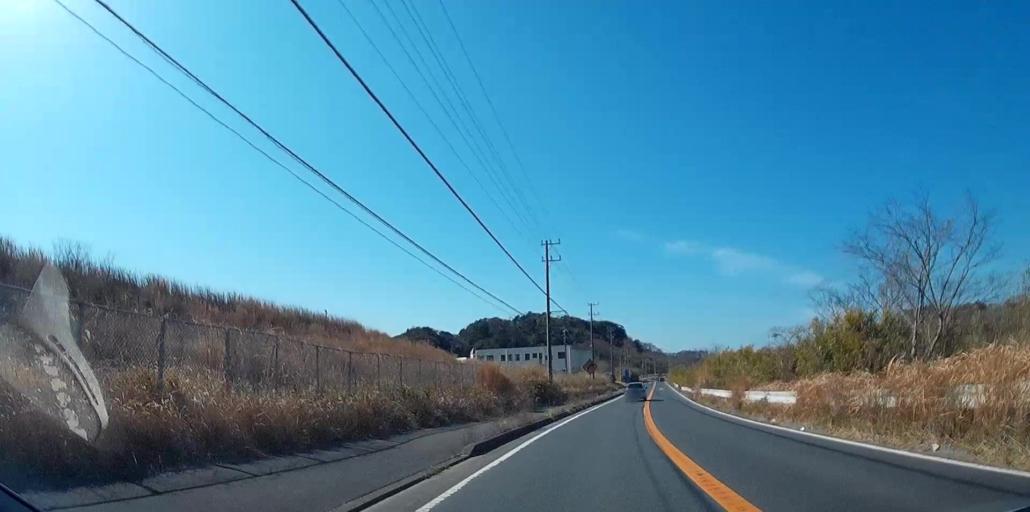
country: JP
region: Chiba
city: Kimitsu
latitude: 35.2318
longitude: 139.8808
